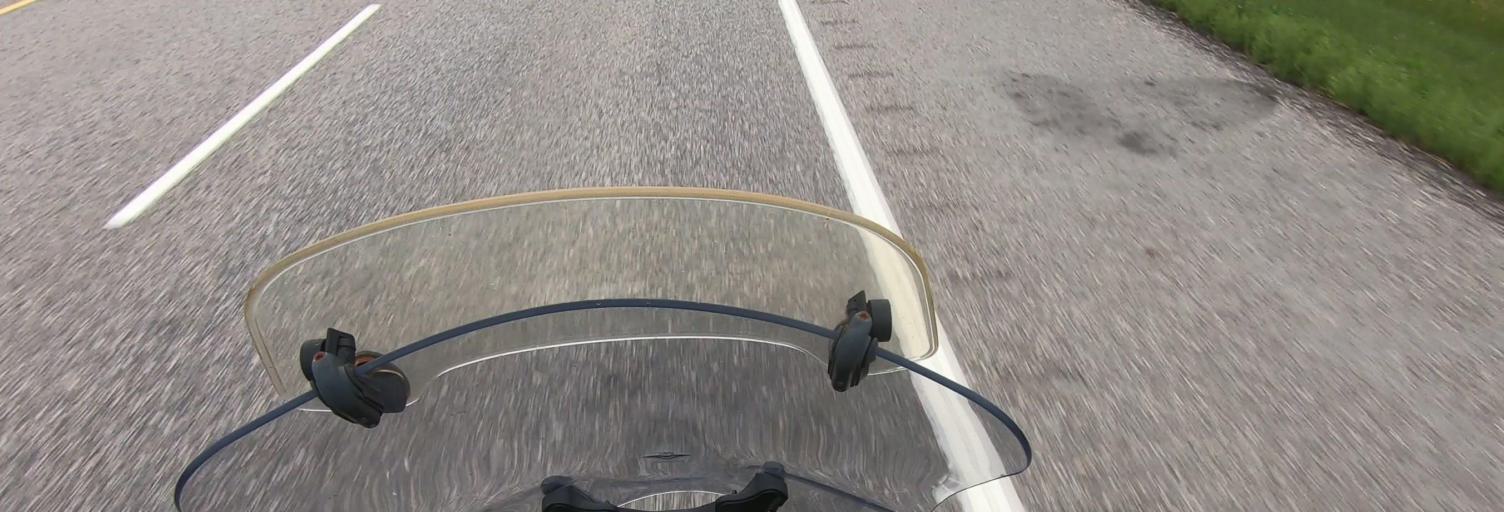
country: CA
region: Manitoba
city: Portage la Prairie
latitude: 49.9752
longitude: -98.6460
